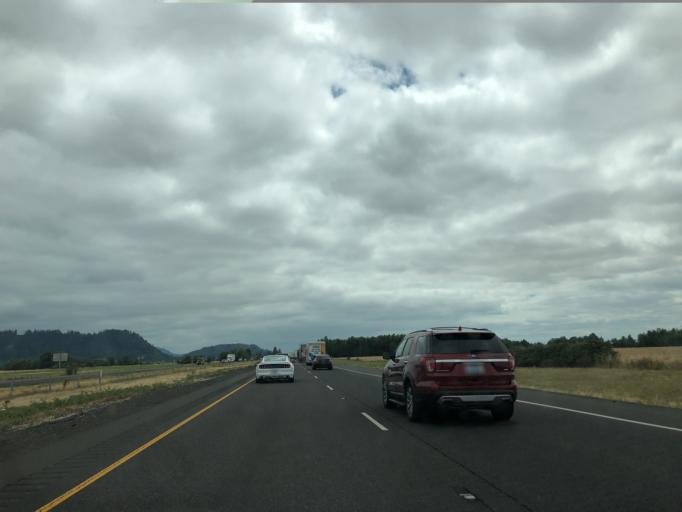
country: US
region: Oregon
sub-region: Lane County
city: Coburg
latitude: 44.2322
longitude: -123.0610
